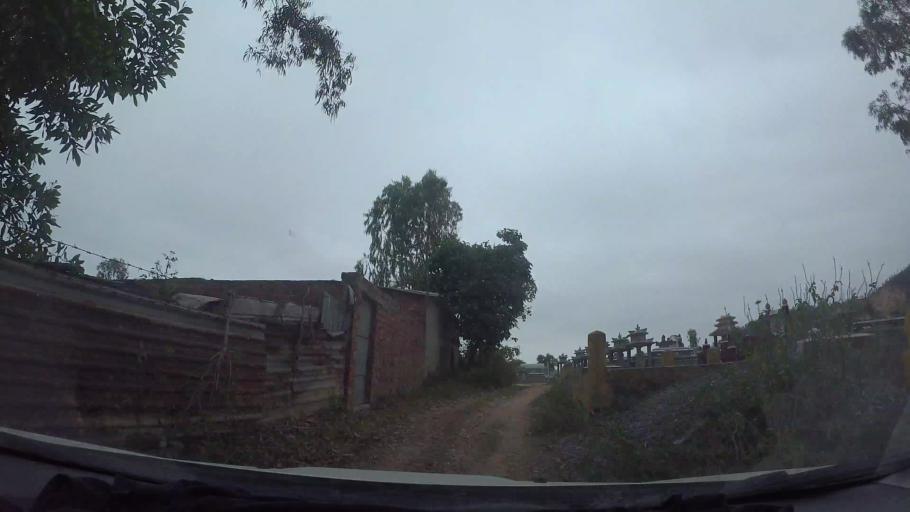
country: VN
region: Da Nang
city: Lien Chieu
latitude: 16.0705
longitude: 108.1378
